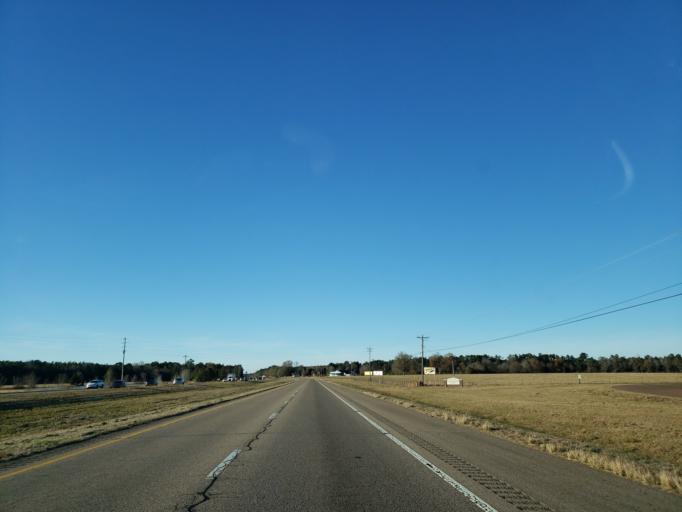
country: US
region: Mississippi
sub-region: Forrest County
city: Rawls Springs
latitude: 31.4444
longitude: -89.4277
